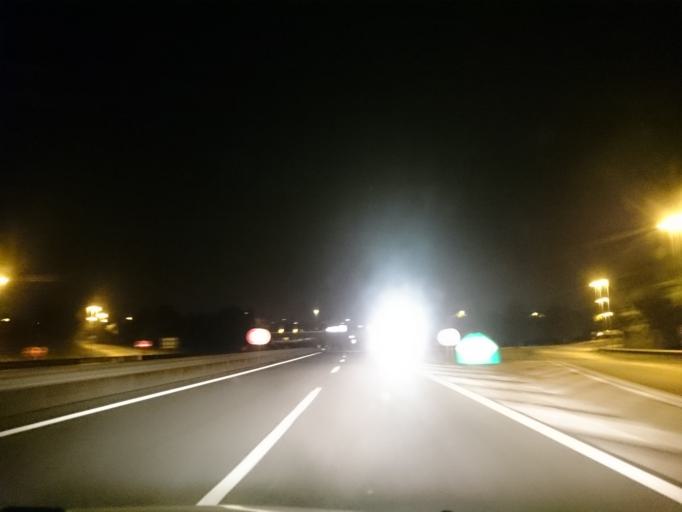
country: FR
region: Pays de la Loire
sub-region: Departement de la Loire-Atlantique
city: Bouguenais
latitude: 47.1730
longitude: -1.6135
